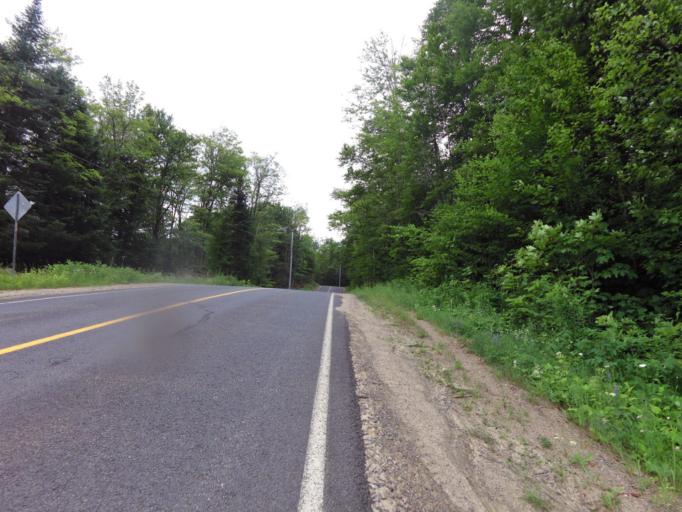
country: CA
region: Quebec
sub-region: Laurentides
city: Brownsburg-Chatham
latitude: 45.8899
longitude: -74.5913
